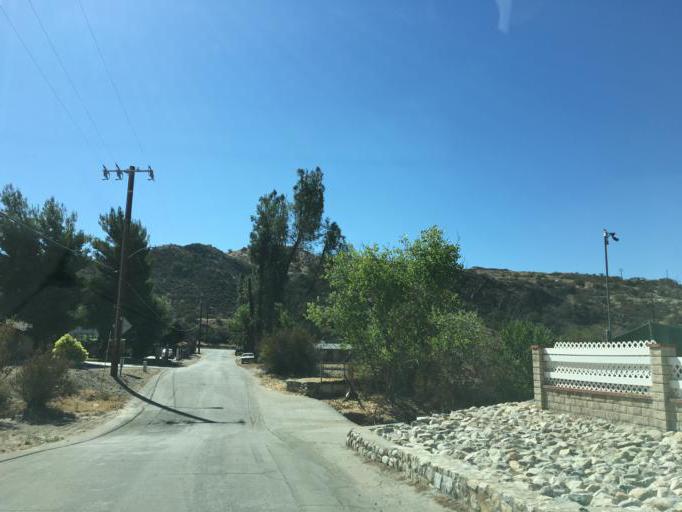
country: US
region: California
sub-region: Los Angeles County
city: Agua Dulce
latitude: 34.4496
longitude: -118.4261
